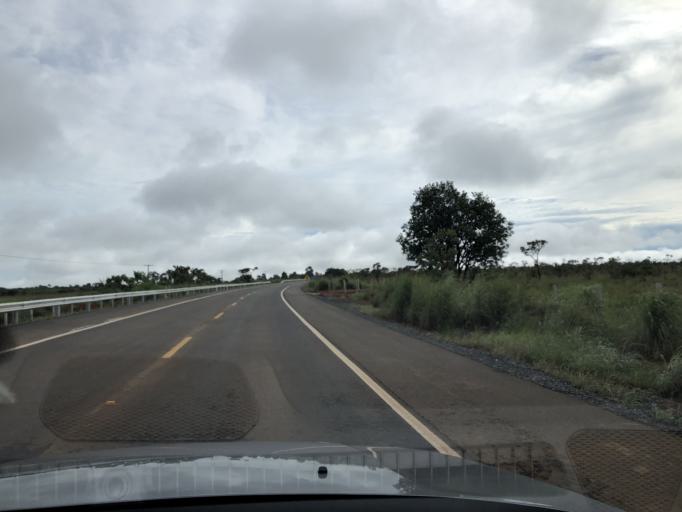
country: BR
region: Federal District
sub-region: Brasilia
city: Brasilia
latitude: -15.6274
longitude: -48.0737
